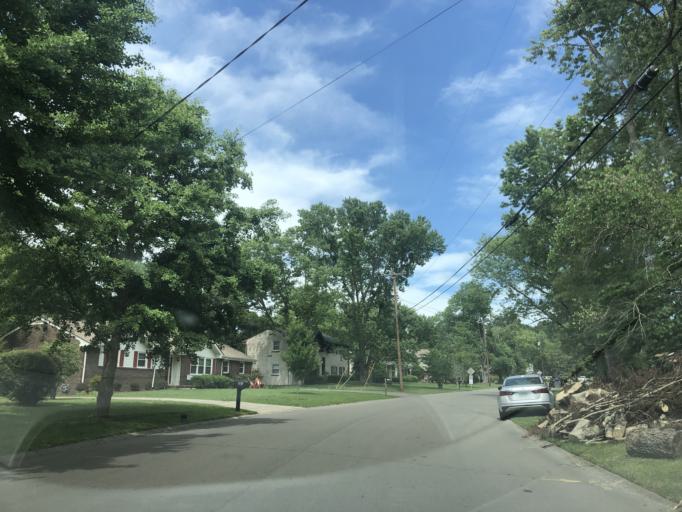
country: US
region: Tennessee
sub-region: Davidson County
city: Belle Meade
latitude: 36.0792
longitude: -86.9418
